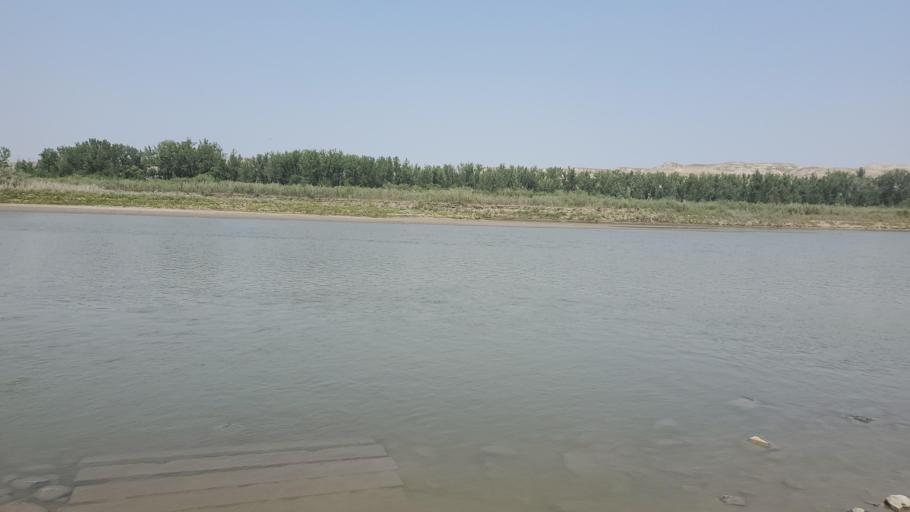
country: CA
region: Alberta
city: Brooks
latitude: 50.7638
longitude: -111.5172
